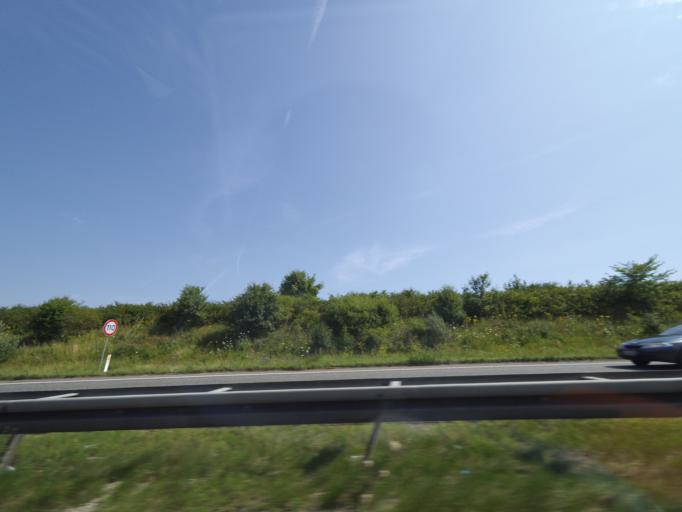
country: DK
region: South Denmark
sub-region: Fredericia Kommune
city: Taulov
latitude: 55.5885
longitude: 9.6051
